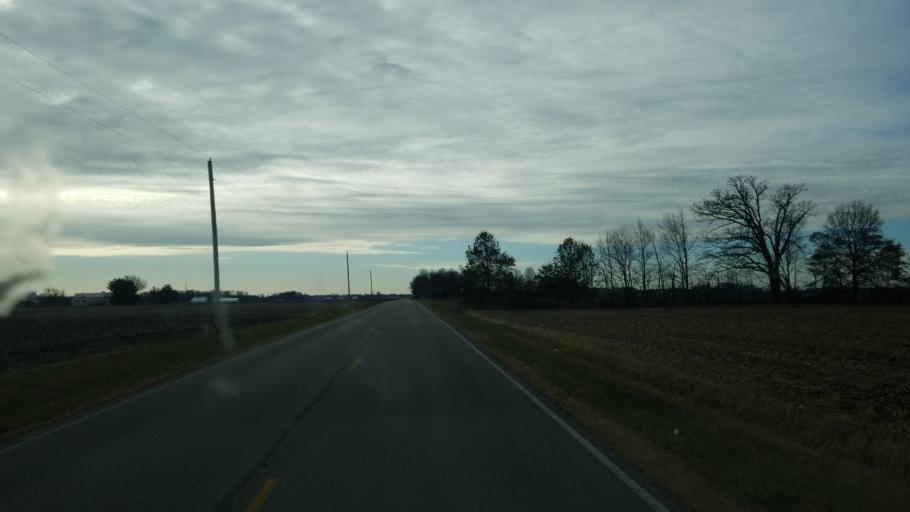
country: US
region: Ohio
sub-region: Marion County
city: Marion
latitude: 40.5947
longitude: -83.0101
